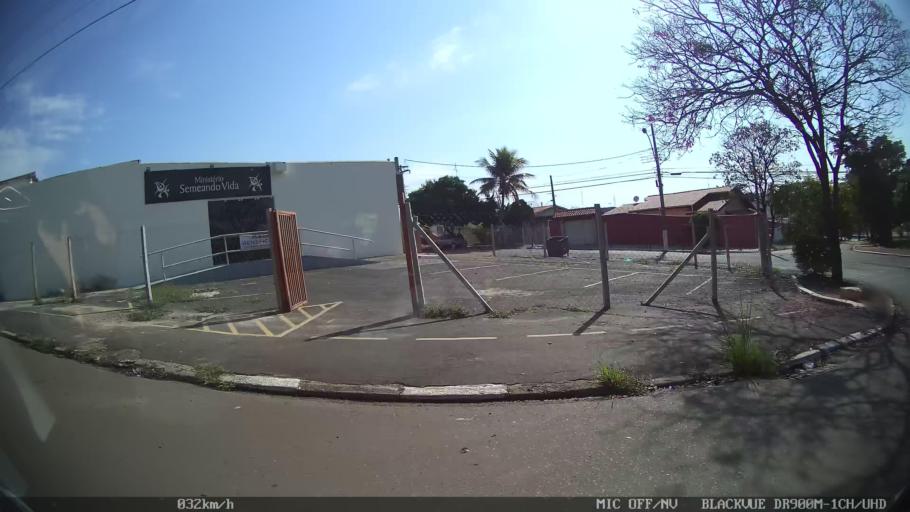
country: BR
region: Sao Paulo
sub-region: Paulinia
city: Paulinia
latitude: -22.7699
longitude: -47.1580
